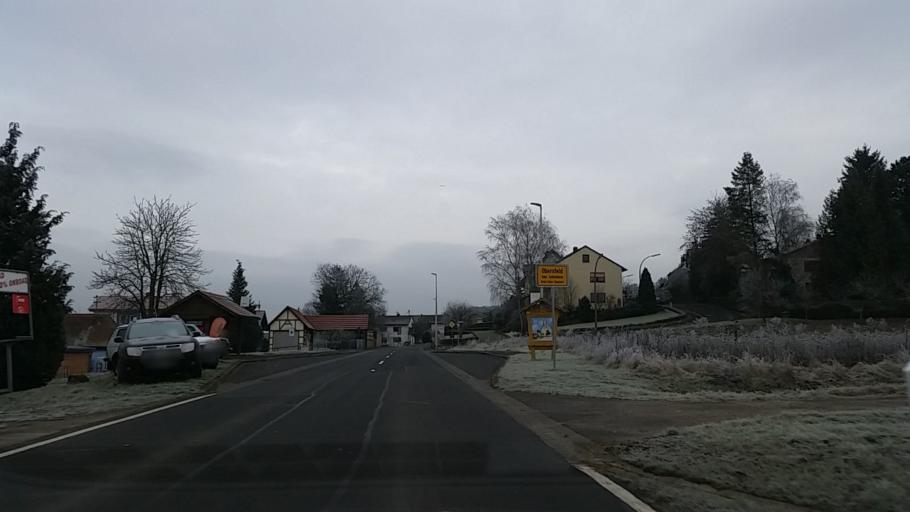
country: DE
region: Bavaria
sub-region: Regierungsbezirk Unterfranken
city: Thungen
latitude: 50.0239
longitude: 9.8896
